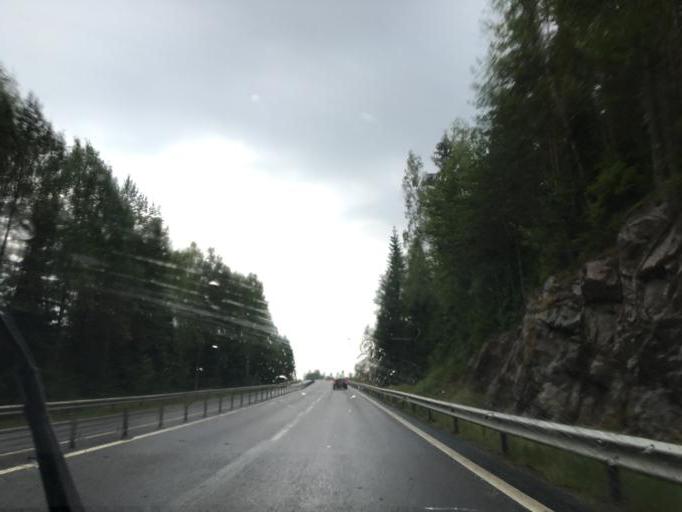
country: SE
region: OEstergoetland
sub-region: Norrkopings Kommun
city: Jursla
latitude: 58.7699
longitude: 16.1663
